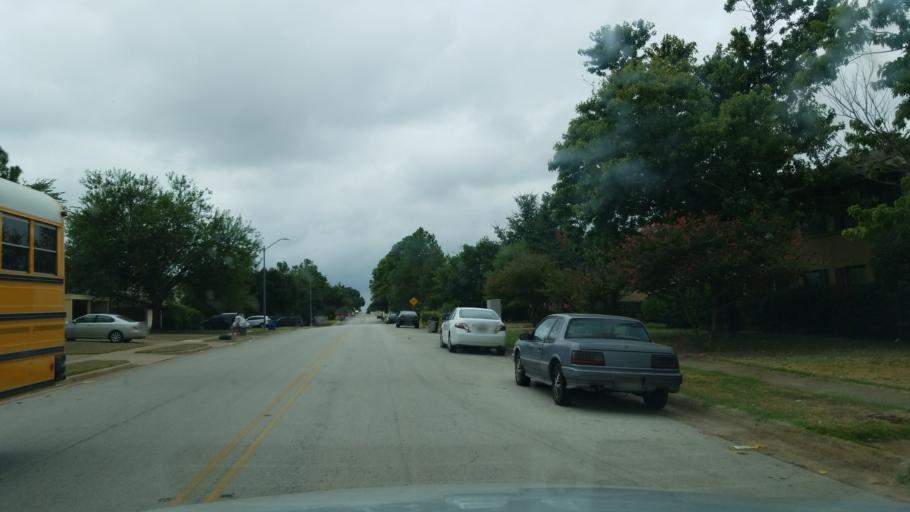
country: US
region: Texas
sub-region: Tarrant County
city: Euless
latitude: 32.8359
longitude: -97.1079
